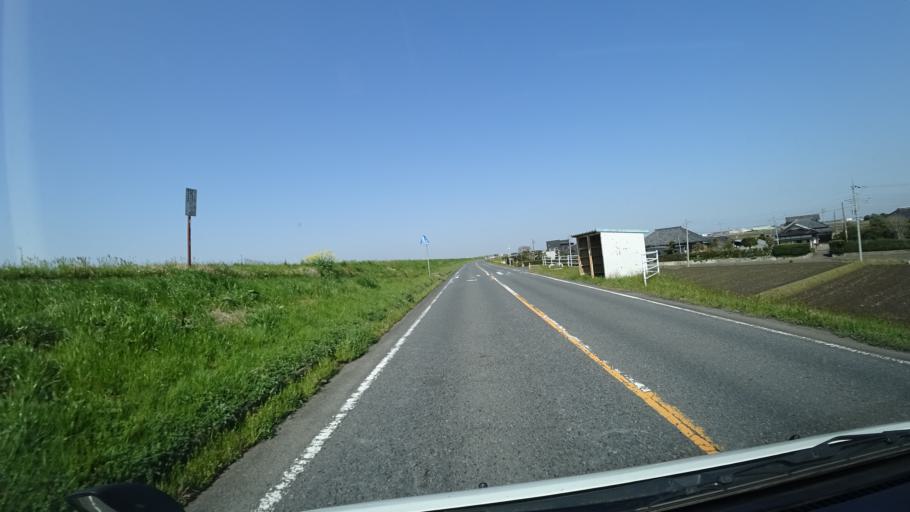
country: JP
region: Chiba
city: Katori-shi
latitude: 35.9128
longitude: 140.4844
